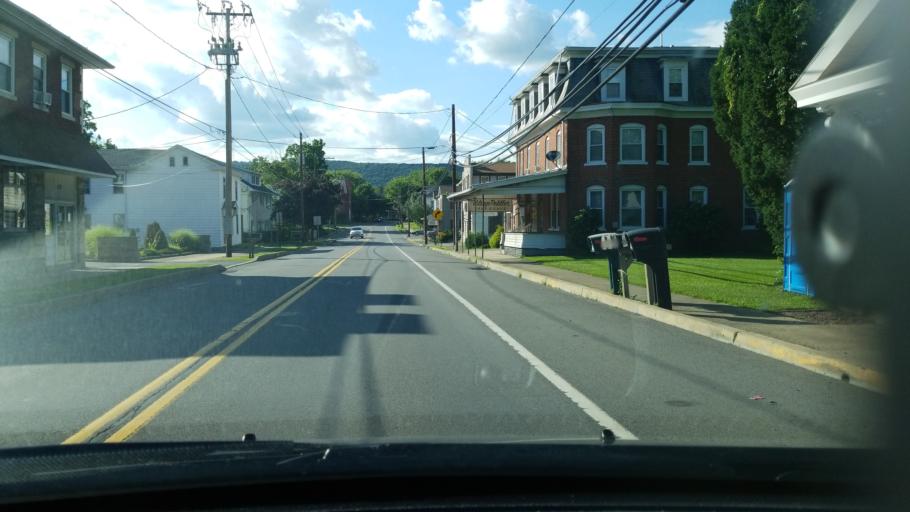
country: US
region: Pennsylvania
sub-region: Northumberland County
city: Elysburg
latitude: 40.8650
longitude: -76.5526
